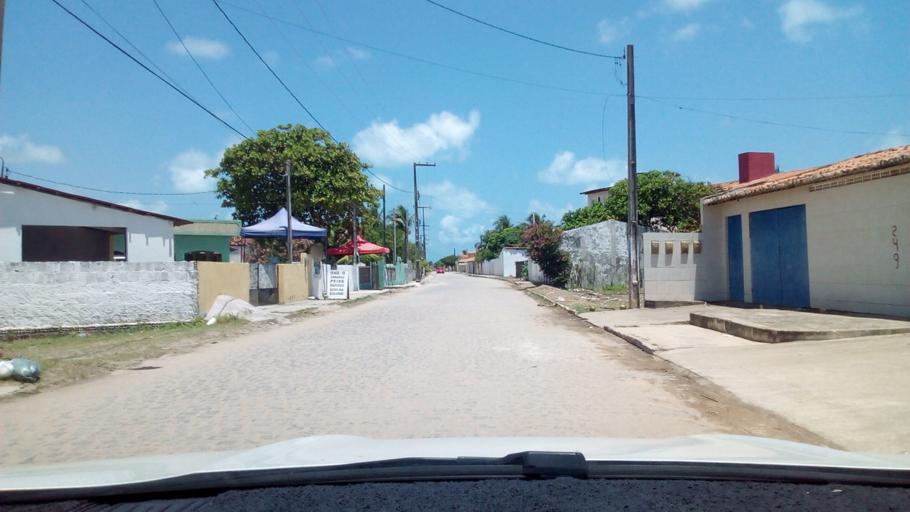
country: BR
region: Paraiba
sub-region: Pitimbu
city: Pitimbu
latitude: -7.5201
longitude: -34.8156
